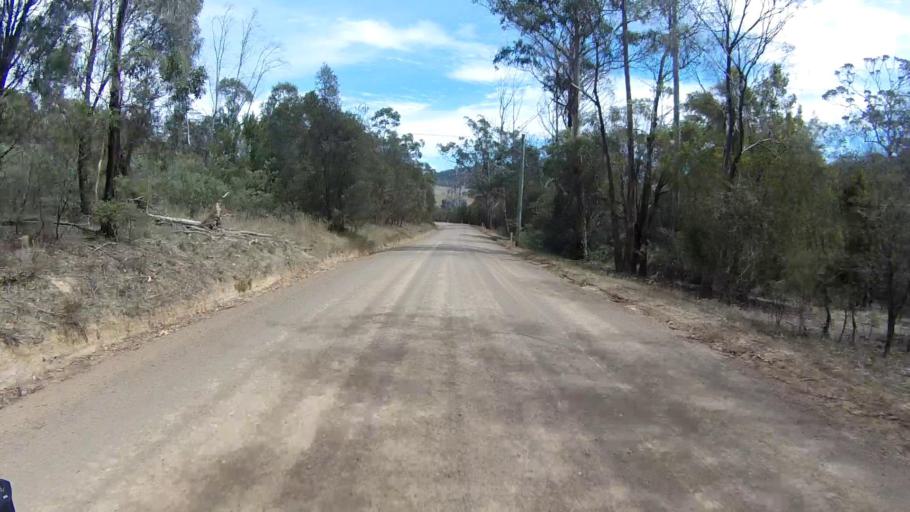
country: AU
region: Tasmania
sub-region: Sorell
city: Sorell
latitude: -42.8021
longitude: 147.6683
